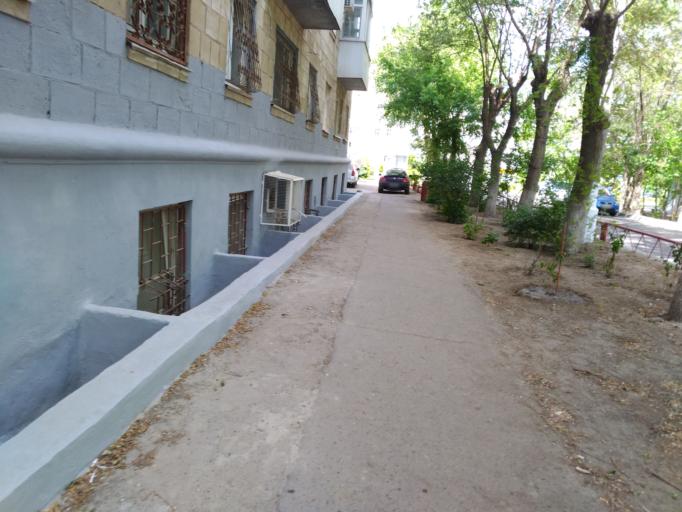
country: RU
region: Volgograd
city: Volgograd
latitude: 48.7207
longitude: 44.5364
